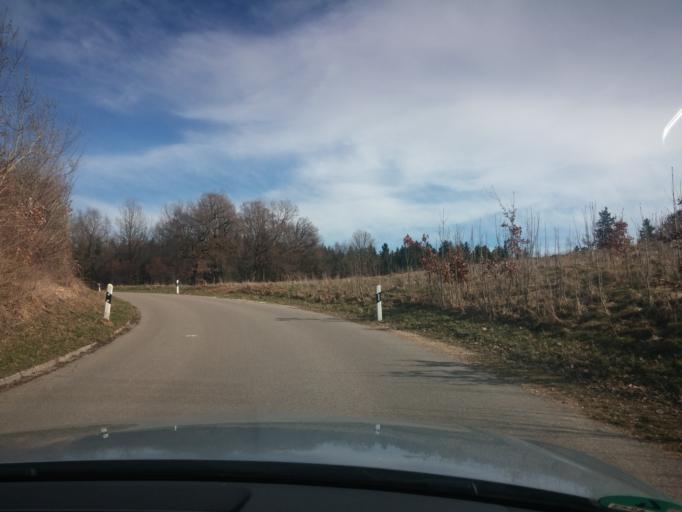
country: DE
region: Baden-Wuerttemberg
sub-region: Tuebingen Region
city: Aitrach
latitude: 47.9401
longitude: 10.1099
